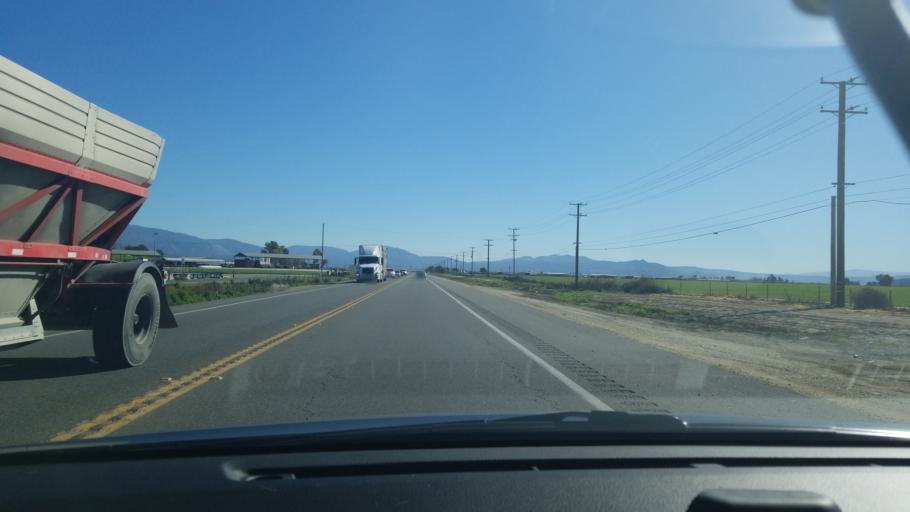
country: US
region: California
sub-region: Riverside County
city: Lakeview
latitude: 33.8310
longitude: -117.0476
